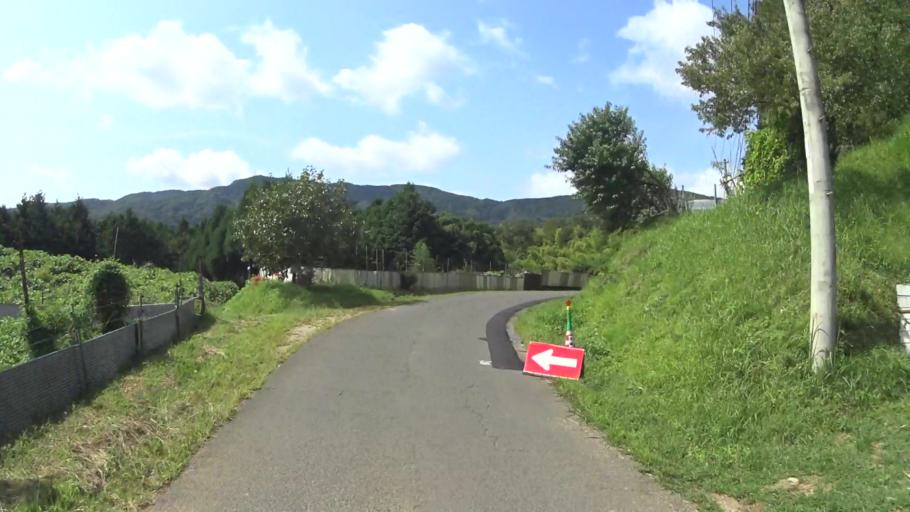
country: JP
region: Kyoto
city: Miyazu
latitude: 35.6749
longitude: 135.2408
